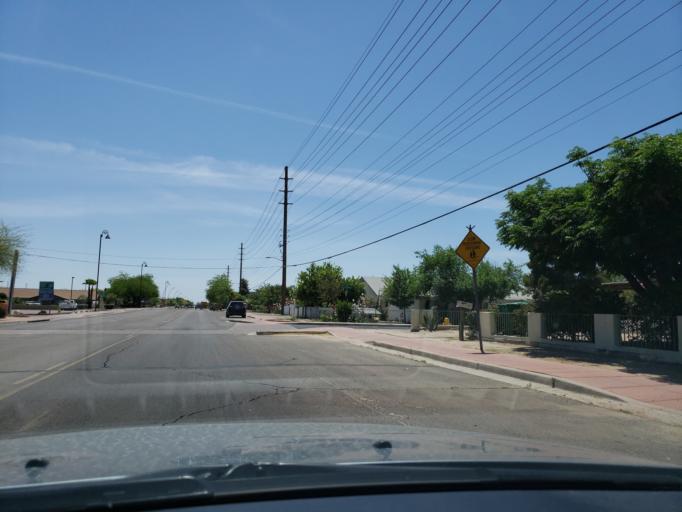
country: US
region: Arizona
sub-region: Maricopa County
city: Guadalupe
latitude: 33.3622
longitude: -111.9632
